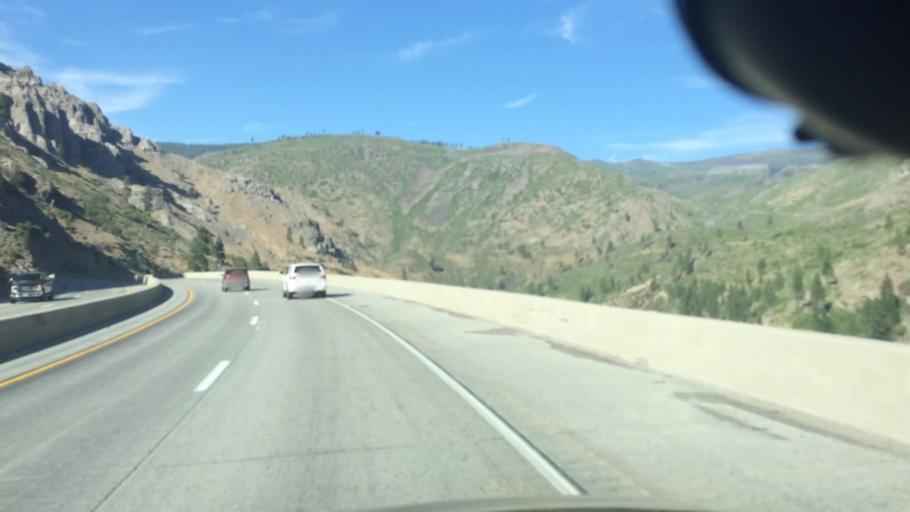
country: US
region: California
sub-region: Placer County
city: Tahoe Vista
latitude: 39.3731
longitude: -120.0331
